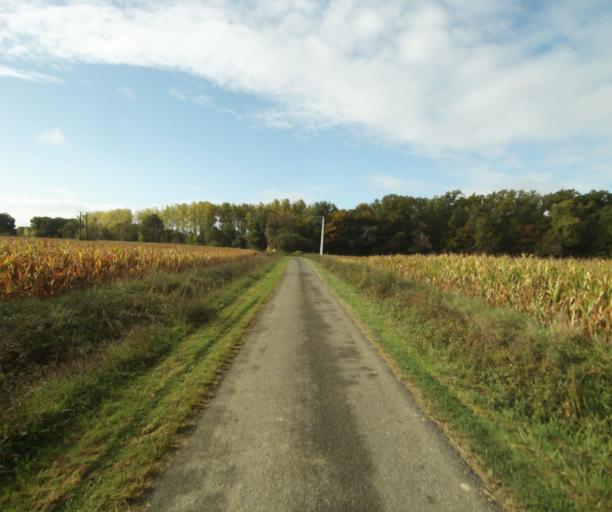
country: FR
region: Midi-Pyrenees
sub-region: Departement du Gers
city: Nogaro
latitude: 43.8050
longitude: -0.0673
